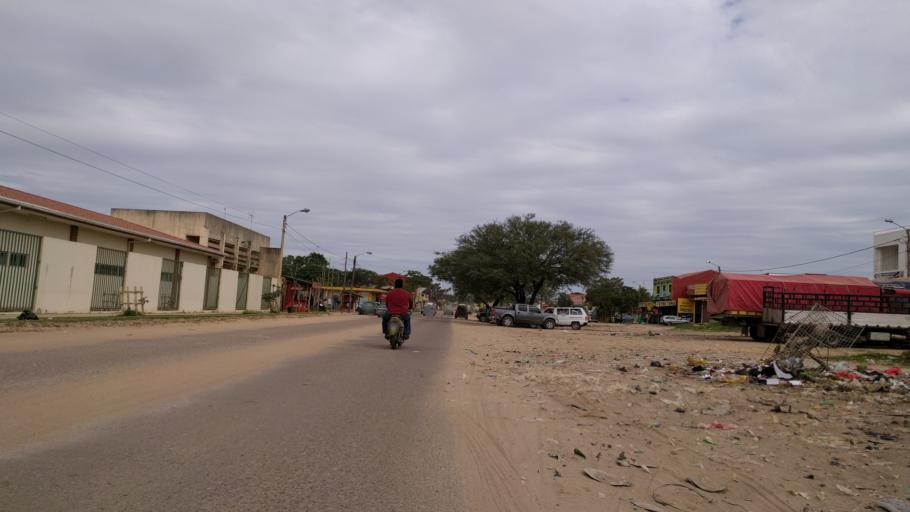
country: BO
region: Santa Cruz
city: Santa Cruz de la Sierra
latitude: -17.8288
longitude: -63.2384
